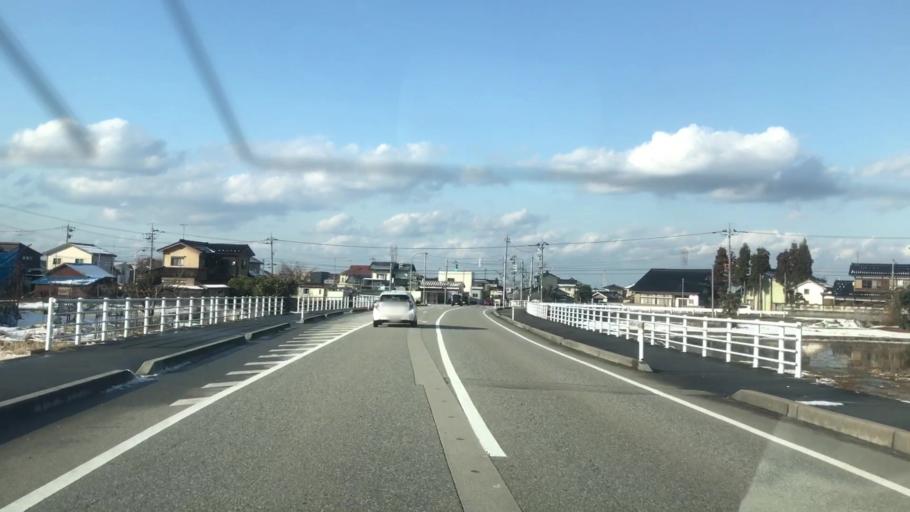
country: JP
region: Toyama
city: Toyama-shi
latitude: 36.6742
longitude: 137.2743
